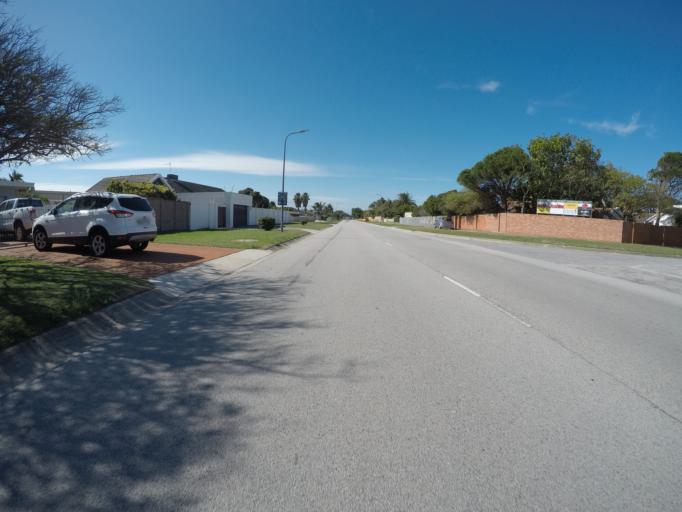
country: ZA
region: Eastern Cape
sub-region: Nelson Mandela Bay Metropolitan Municipality
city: Port Elizabeth
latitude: -33.9921
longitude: 25.6576
